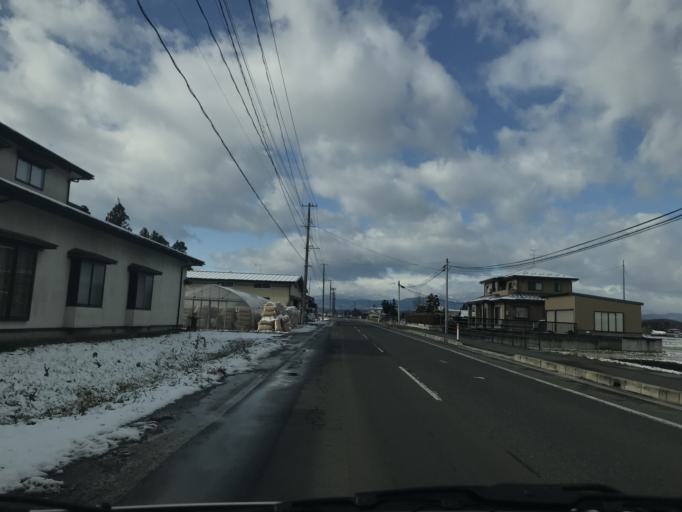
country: JP
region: Iwate
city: Mizusawa
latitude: 39.1626
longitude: 141.1108
